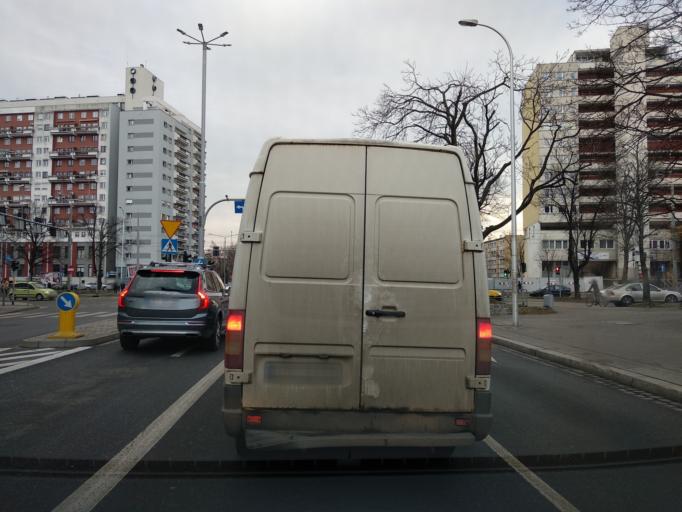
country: PL
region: Lower Silesian Voivodeship
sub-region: Powiat wroclawski
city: Wroclaw
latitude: 51.0935
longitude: 17.0195
